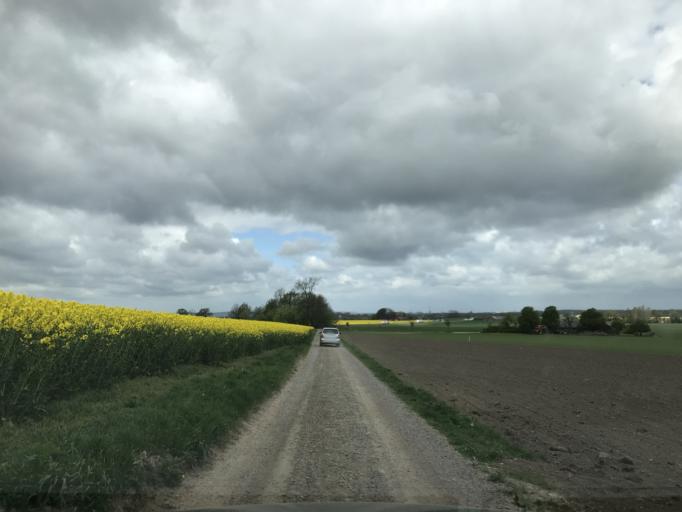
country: SE
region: Skane
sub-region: Helsingborg
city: Glumslov
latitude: 55.9551
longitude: 12.8100
